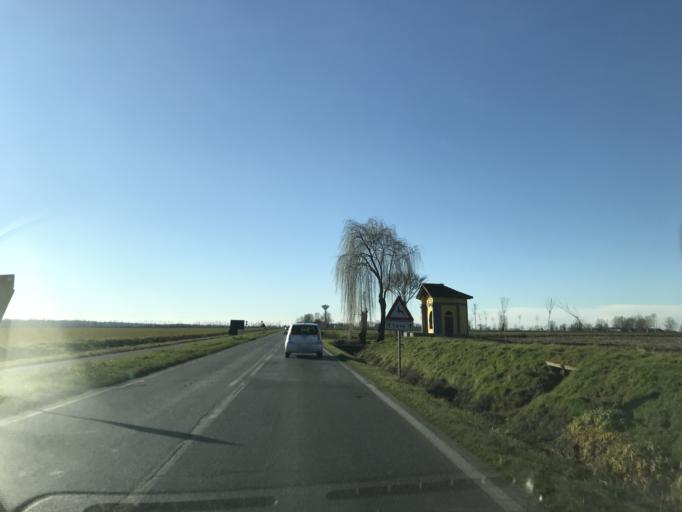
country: IT
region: Lombardy
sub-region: Provincia di Lodi
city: Borghetto Lodigiano
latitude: 45.2140
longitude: 9.4913
